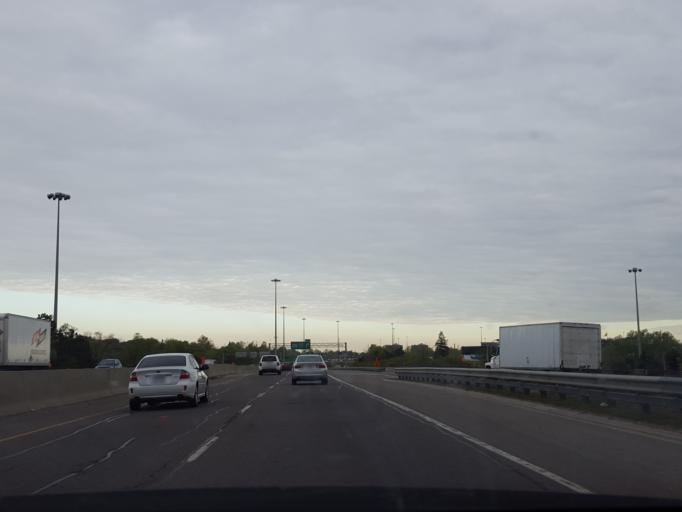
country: CA
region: Ontario
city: Etobicoke
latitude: 43.7114
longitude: -79.5047
